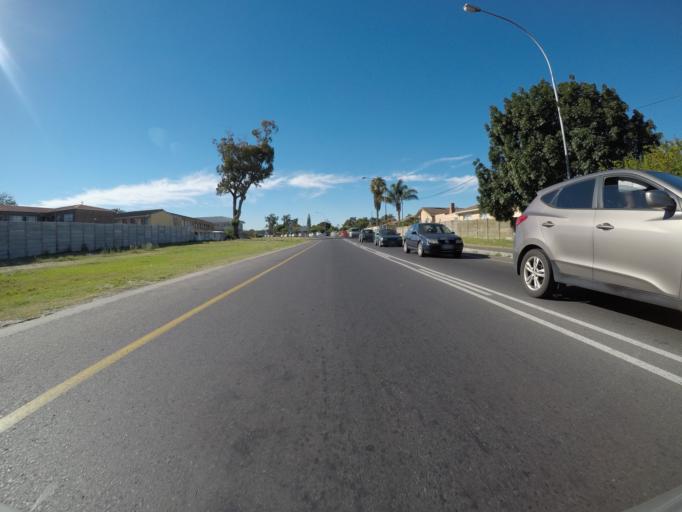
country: ZA
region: Western Cape
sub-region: City of Cape Town
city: Kraaifontein
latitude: -33.9366
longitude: 18.6768
